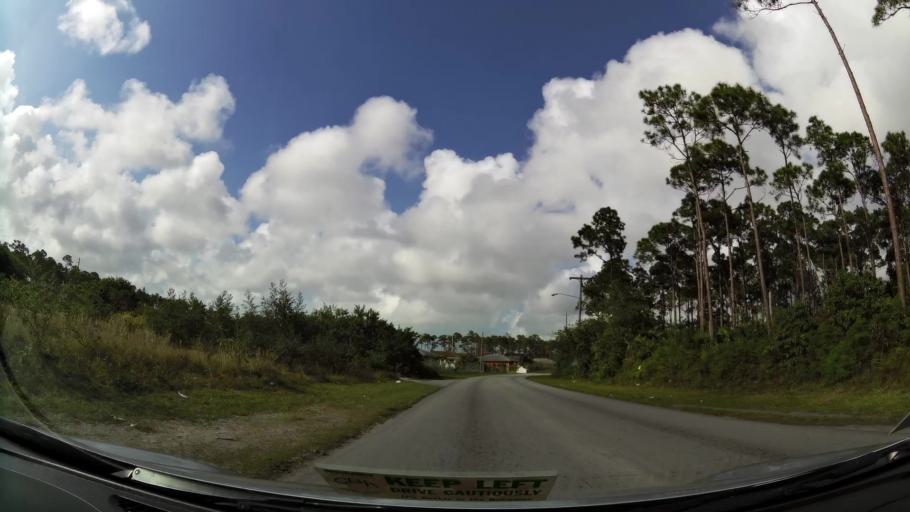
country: BS
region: Freeport
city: Freeport
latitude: 26.5230
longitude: -78.6899
